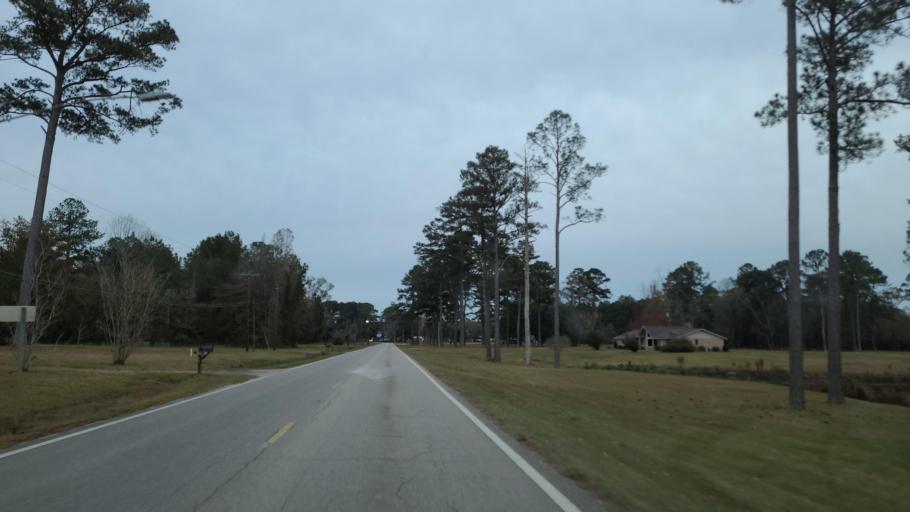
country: US
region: Mississippi
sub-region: Clarke County
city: Stonewall
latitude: 32.0456
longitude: -88.8916
